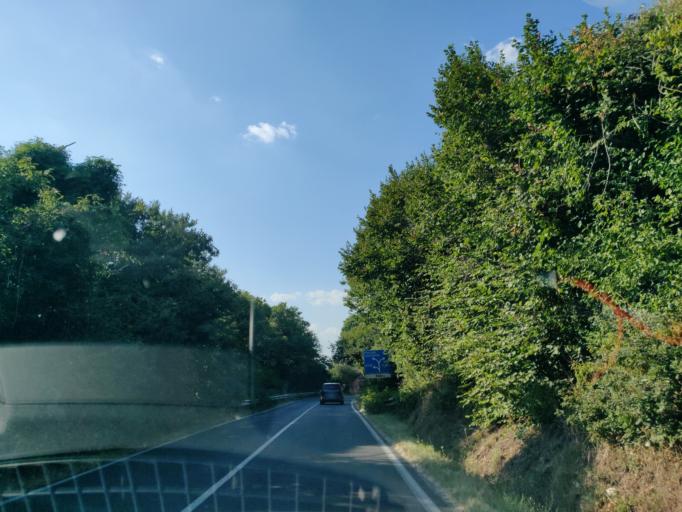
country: IT
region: Latium
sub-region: Provincia di Viterbo
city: Latera
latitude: 42.6294
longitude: 11.8363
